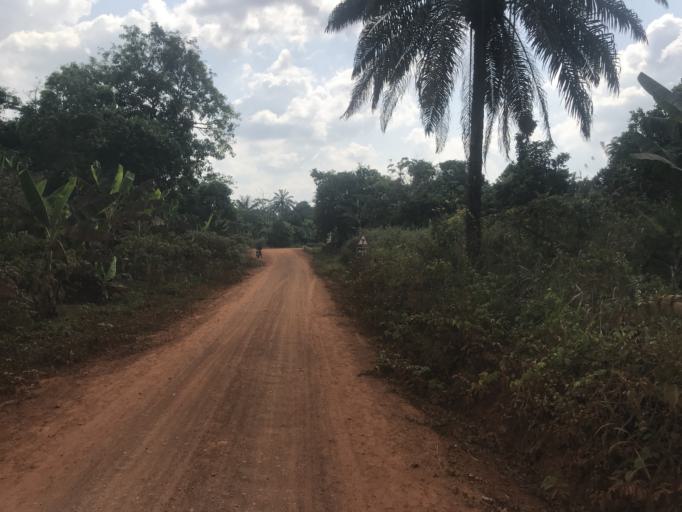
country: NG
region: Osun
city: Ibokun
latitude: 7.7977
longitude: 4.6866
